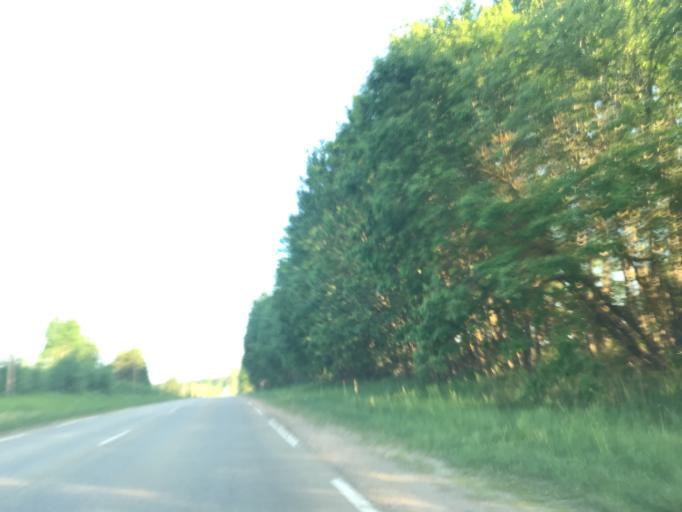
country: LV
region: Baldone
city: Baldone
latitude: 56.7027
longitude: 24.3793
